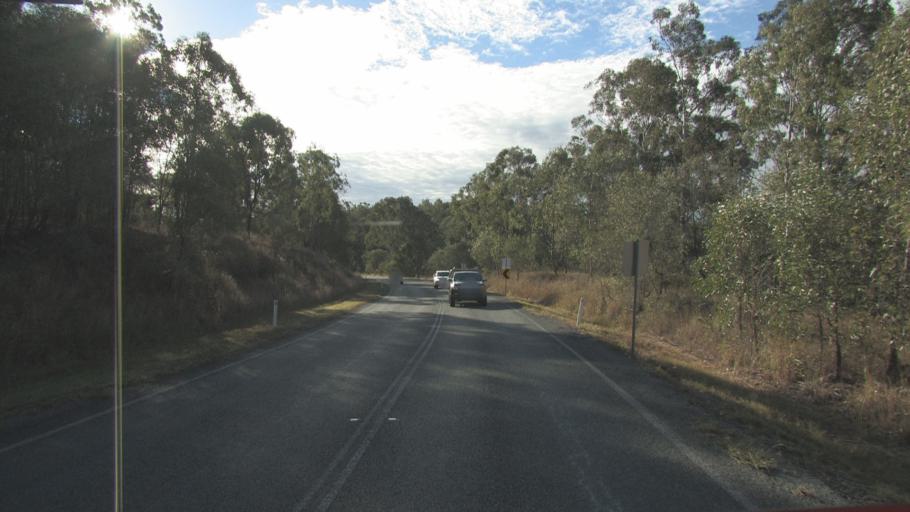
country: AU
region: Queensland
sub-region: Logan
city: Cedar Vale
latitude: -27.8947
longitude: 153.0878
